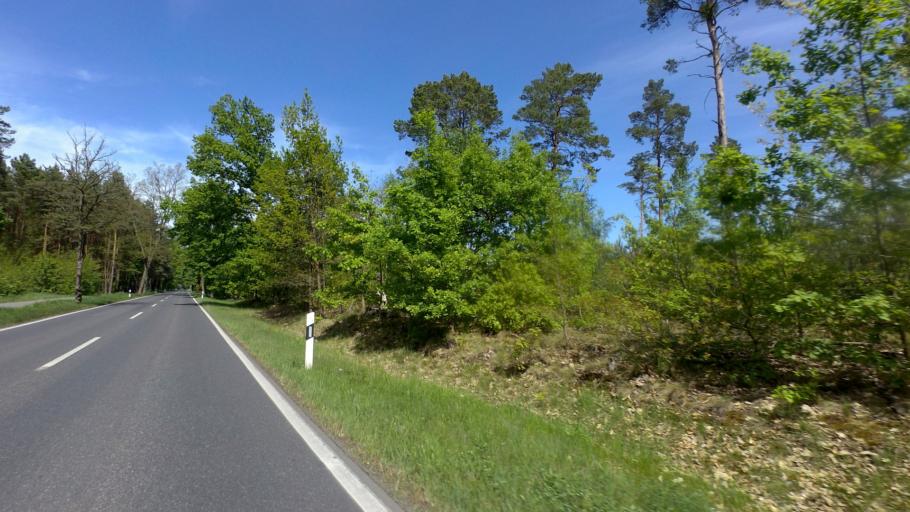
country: DE
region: Brandenburg
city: Sperenberg
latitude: 52.1563
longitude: 13.3657
